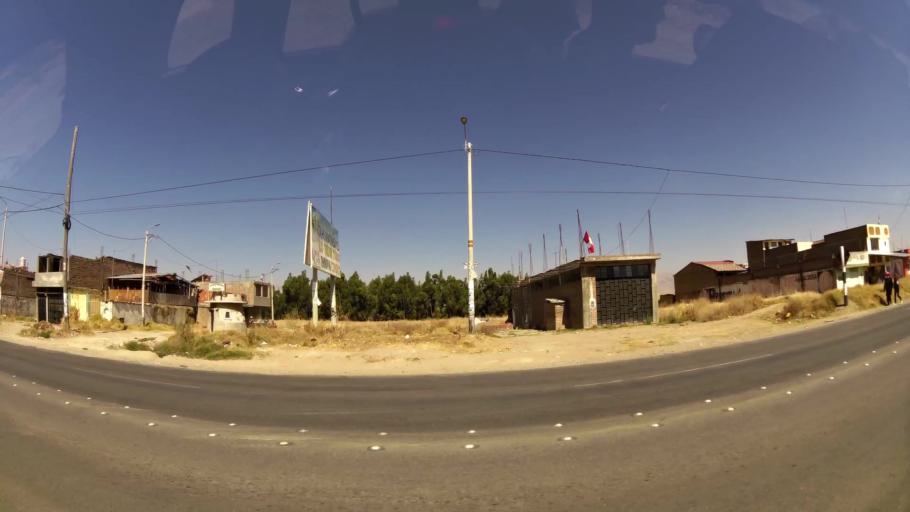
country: PE
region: Junin
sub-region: Provincia de Huancayo
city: San Agustin
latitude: -11.9779
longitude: -75.2648
